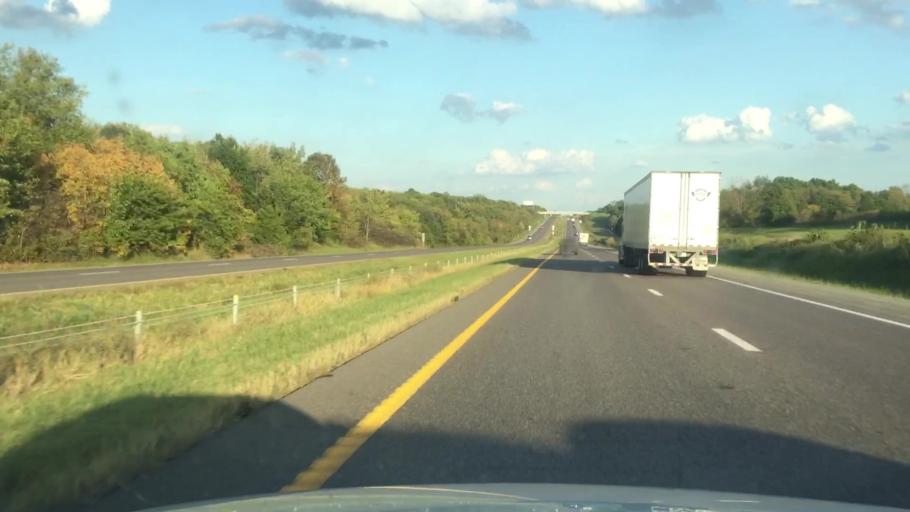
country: US
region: Missouri
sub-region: Saline County
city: Marshall
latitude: 38.9574
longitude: -93.1543
